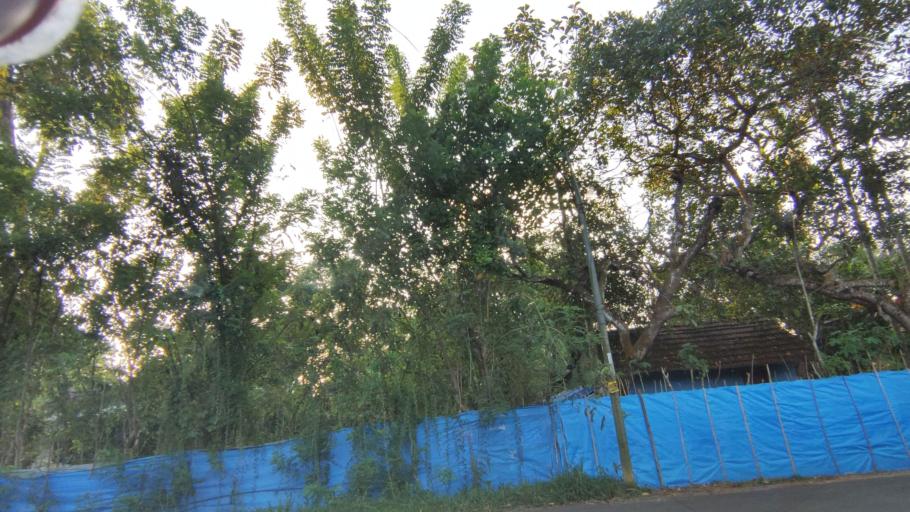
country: IN
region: Kerala
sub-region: Alappuzha
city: Shertallai
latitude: 9.6531
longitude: 76.3486
